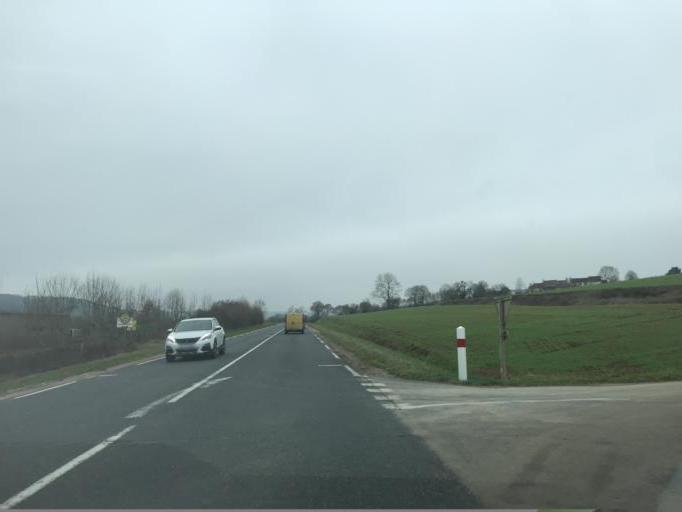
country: FR
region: Bourgogne
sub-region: Departement de l'Yonne
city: Avallon
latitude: 47.5092
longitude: 3.8485
